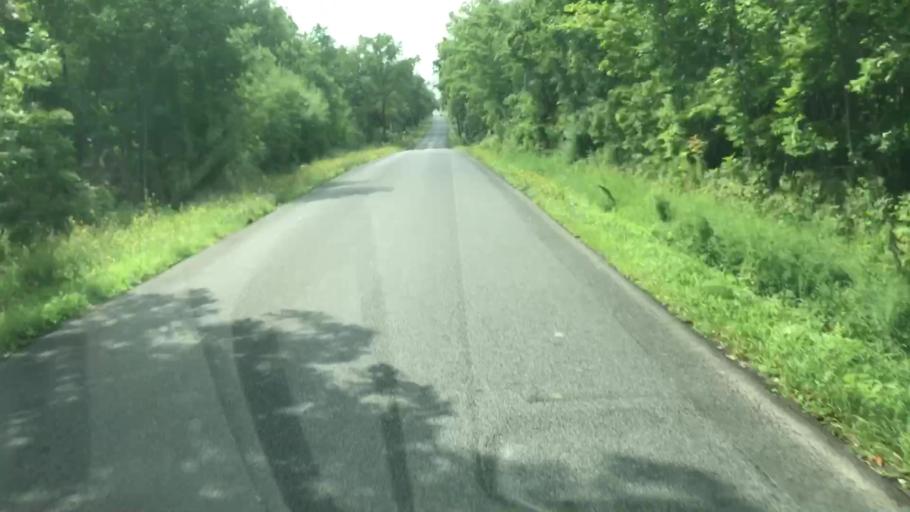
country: US
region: New York
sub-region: Cayuga County
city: Melrose Park
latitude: 42.9255
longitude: -76.5082
